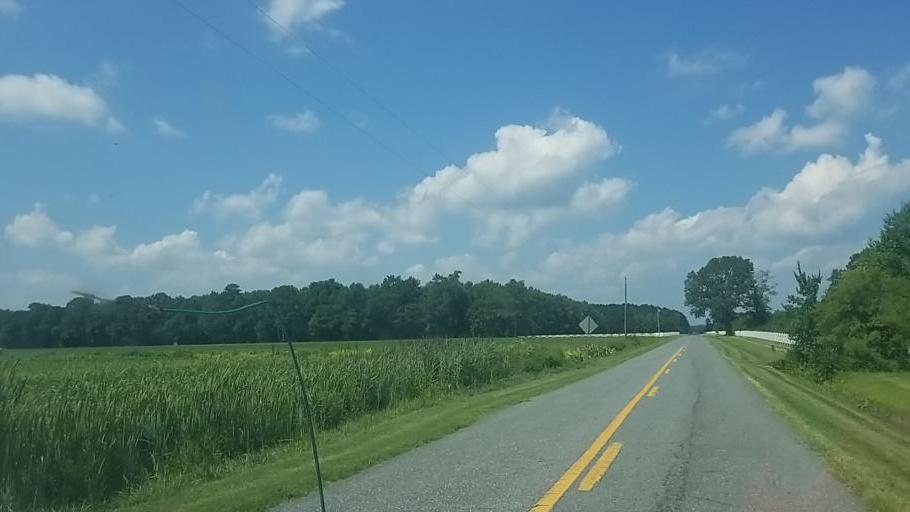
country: US
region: Maryland
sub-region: Wicomico County
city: Hebron
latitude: 38.4495
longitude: -75.8491
